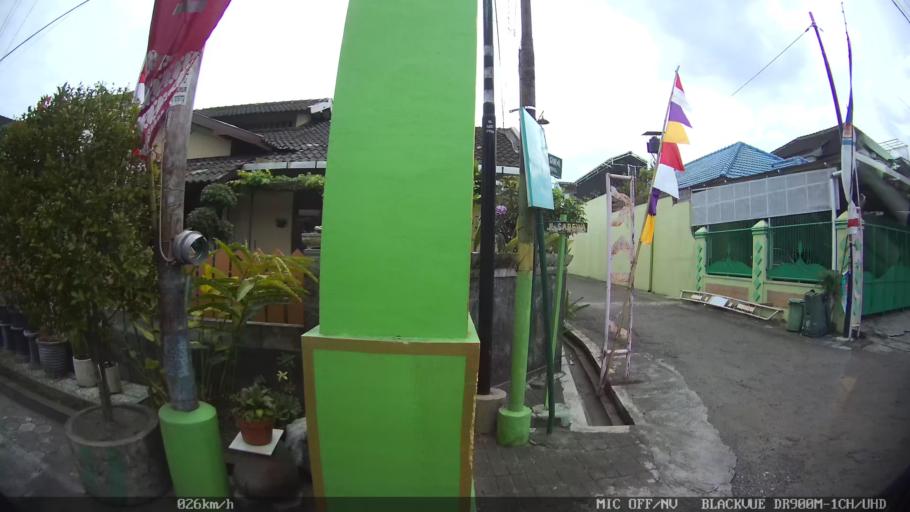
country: ID
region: Daerah Istimewa Yogyakarta
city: Yogyakarta
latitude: -7.7940
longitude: 110.3982
